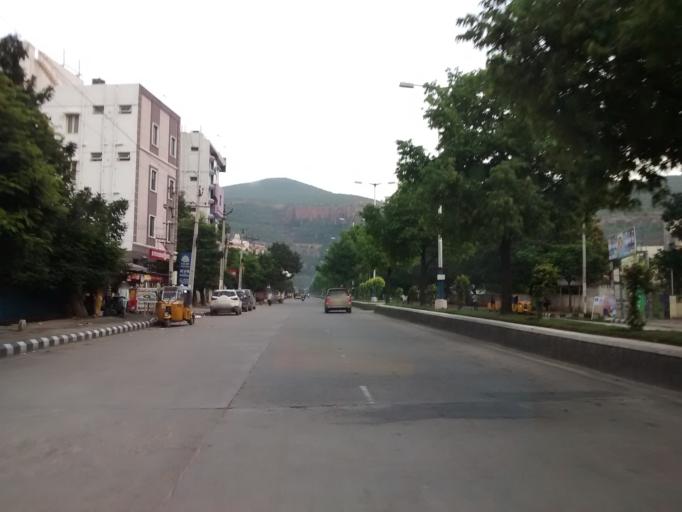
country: IN
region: Andhra Pradesh
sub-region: Chittoor
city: Akkarampalle
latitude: 13.6488
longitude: 79.4251
